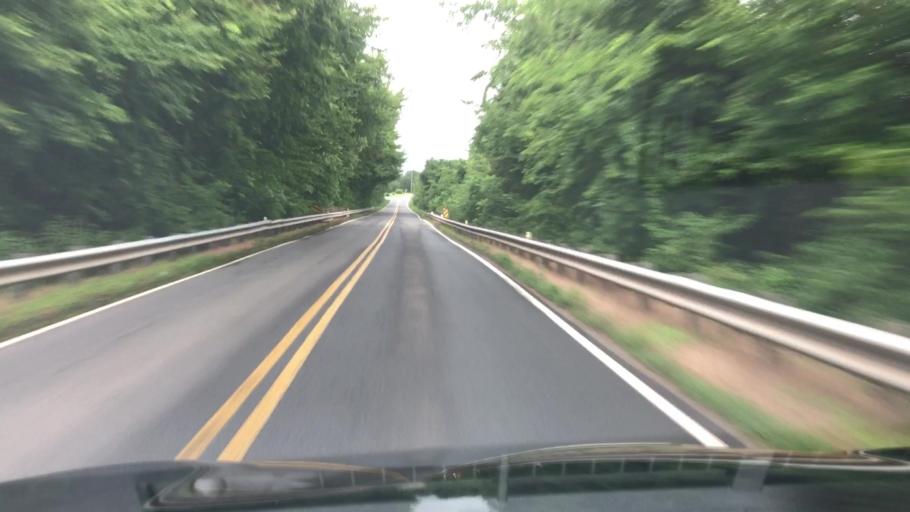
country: US
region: Virginia
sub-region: Prince William County
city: Nokesville
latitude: 38.6071
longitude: -77.6056
